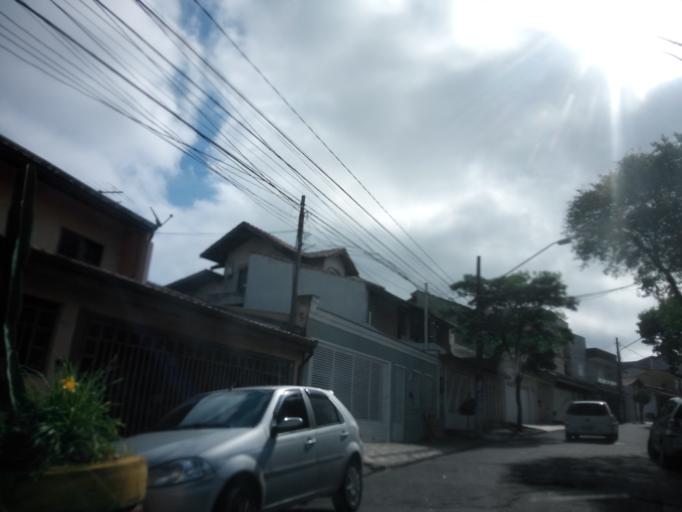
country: BR
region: Sao Paulo
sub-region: Sao Bernardo Do Campo
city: Sao Bernardo do Campo
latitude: -23.7283
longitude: -46.5688
